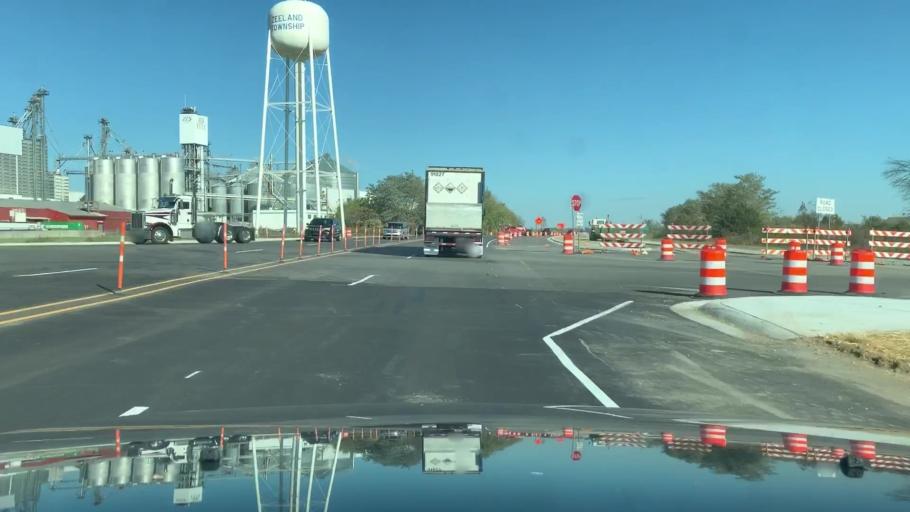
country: US
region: Michigan
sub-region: Ottawa County
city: Zeeland
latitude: 42.8122
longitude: -85.9901
